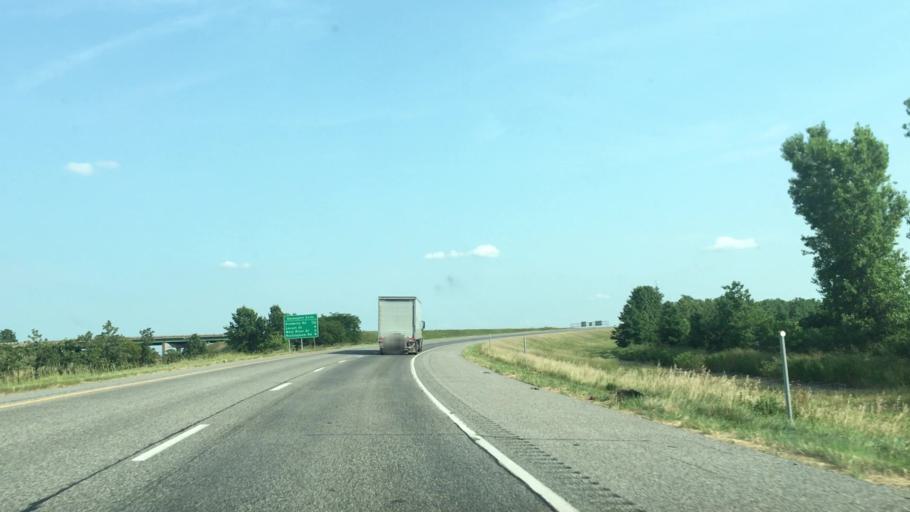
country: US
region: Iowa
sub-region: Scott County
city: Walcott
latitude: 41.6021
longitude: -90.6792
